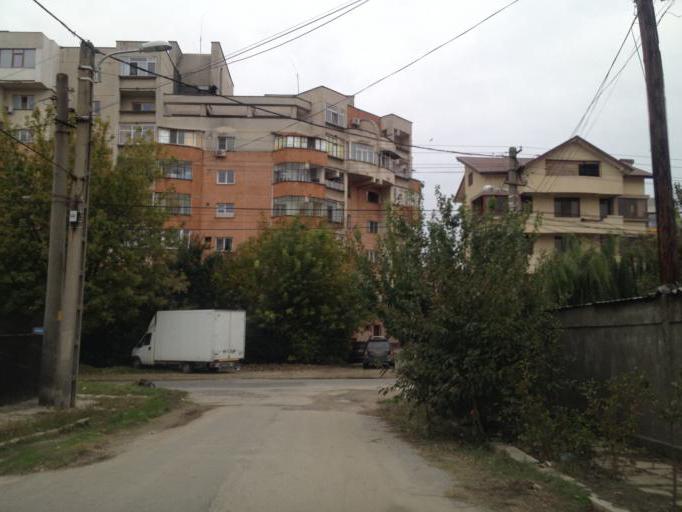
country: RO
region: Dolj
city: Craiova
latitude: 44.3332
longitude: 23.7741
